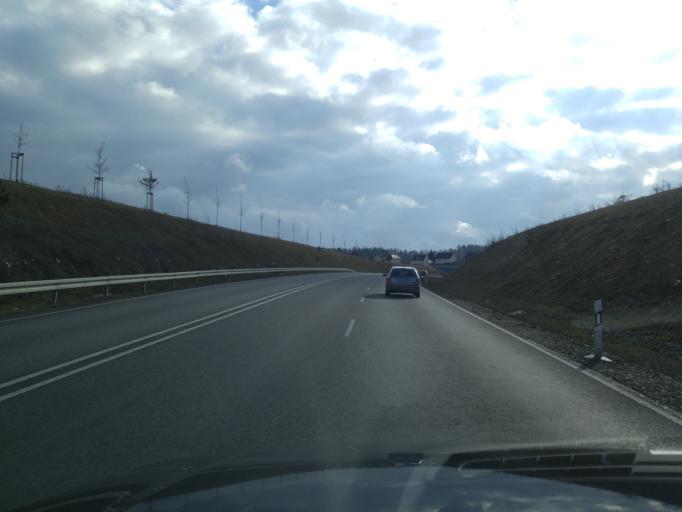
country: DE
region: Saxony
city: Hirschfeld
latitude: 50.6532
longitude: 12.4459
